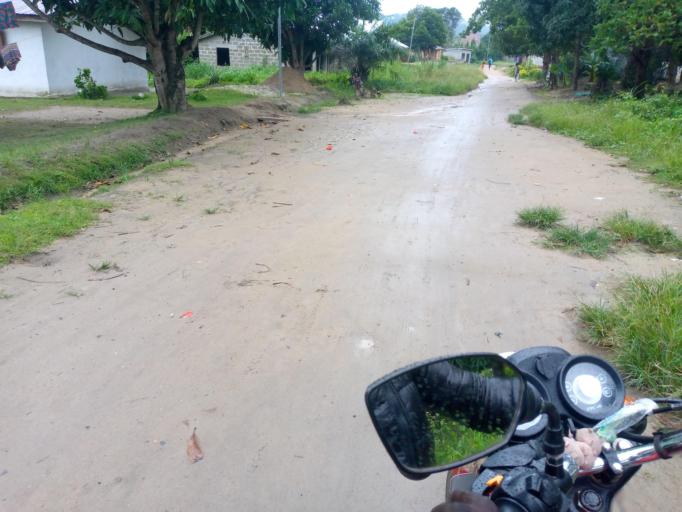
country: SL
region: Eastern Province
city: Kenema
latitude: 7.8416
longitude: -11.2053
